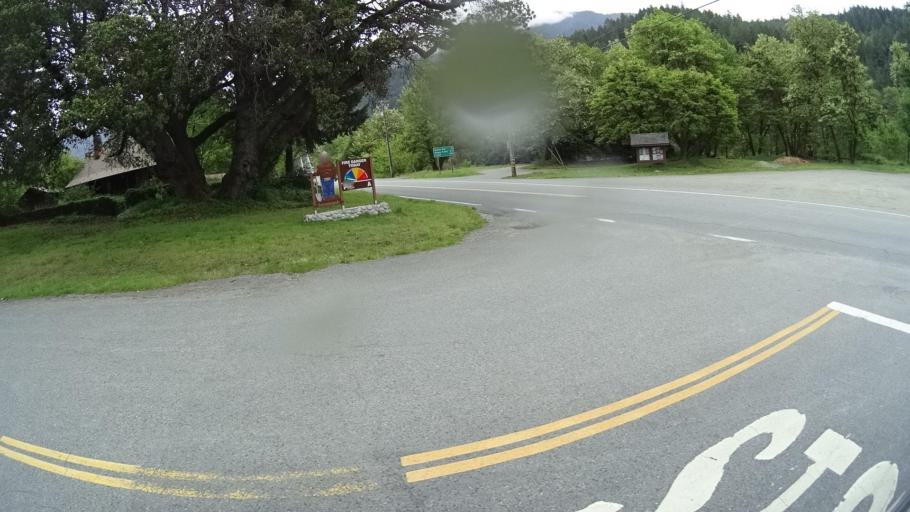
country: US
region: California
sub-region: Humboldt County
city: Willow Creek
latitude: 41.3029
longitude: -123.5376
